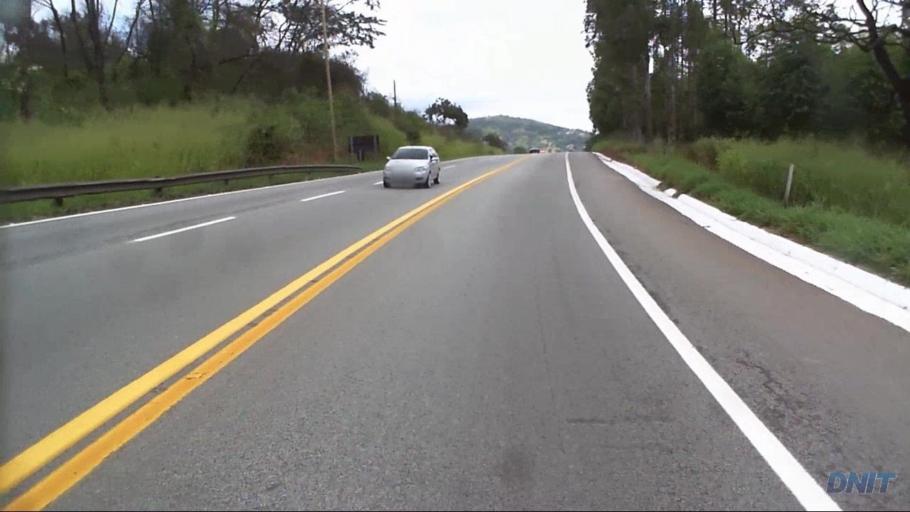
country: BR
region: Minas Gerais
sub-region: Caete
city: Caete
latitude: -19.7880
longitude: -43.7365
